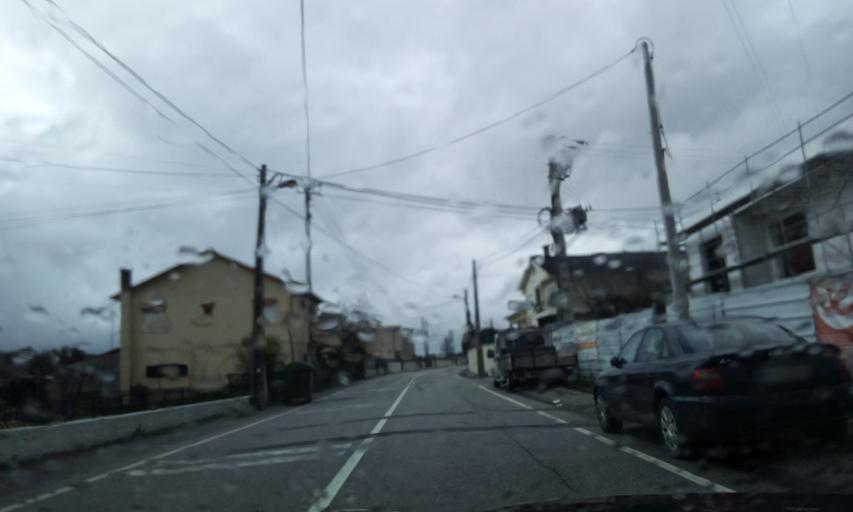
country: PT
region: Viseu
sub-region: Viseu
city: Rio de Loba
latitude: 40.6350
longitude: -7.8662
